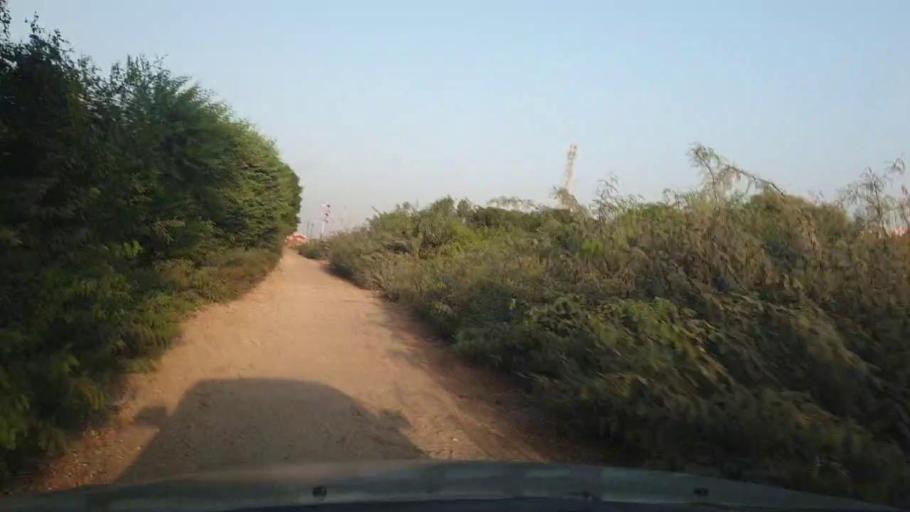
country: PK
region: Sindh
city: Tando Jam
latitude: 25.4288
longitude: 68.5225
